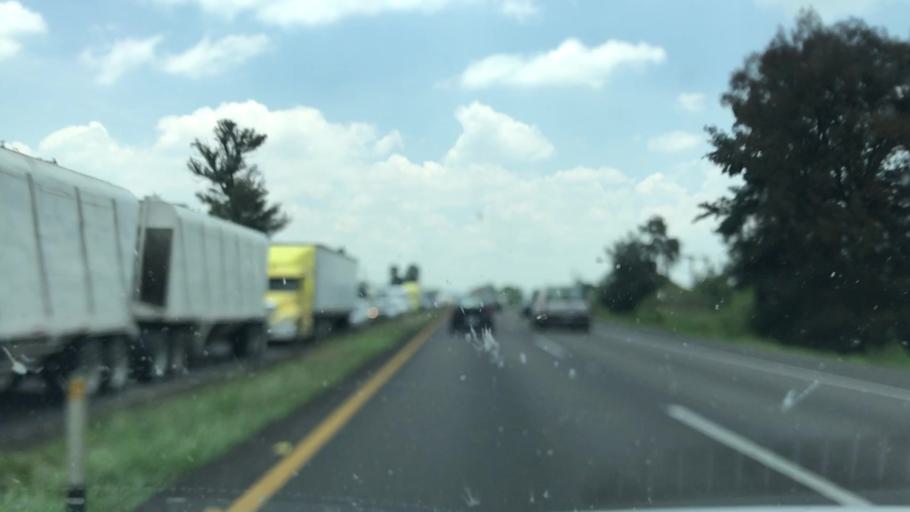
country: MX
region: Guanajuato
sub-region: Irapuato
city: Colonia Morelos de Guadalupe de Rivera
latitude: 20.5995
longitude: -101.4180
